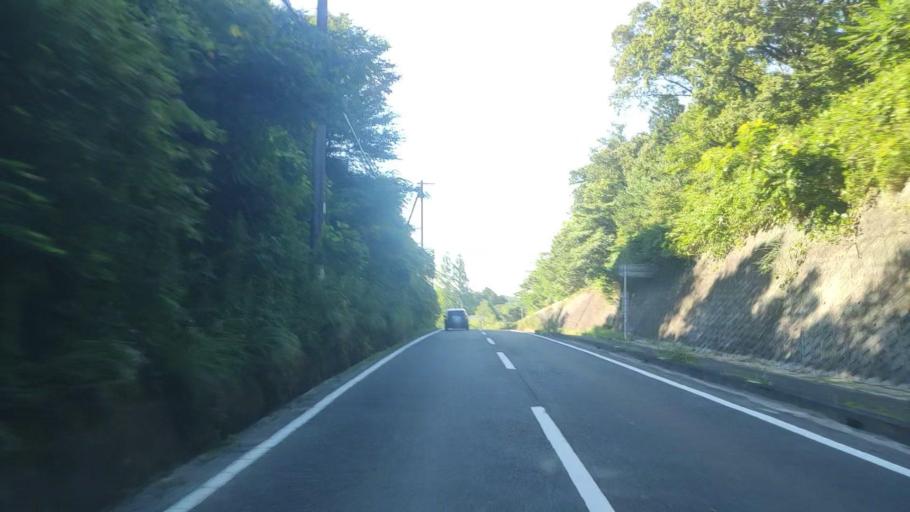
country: JP
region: Shiga Prefecture
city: Minakuchicho-matoba
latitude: 34.9451
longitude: 136.2049
